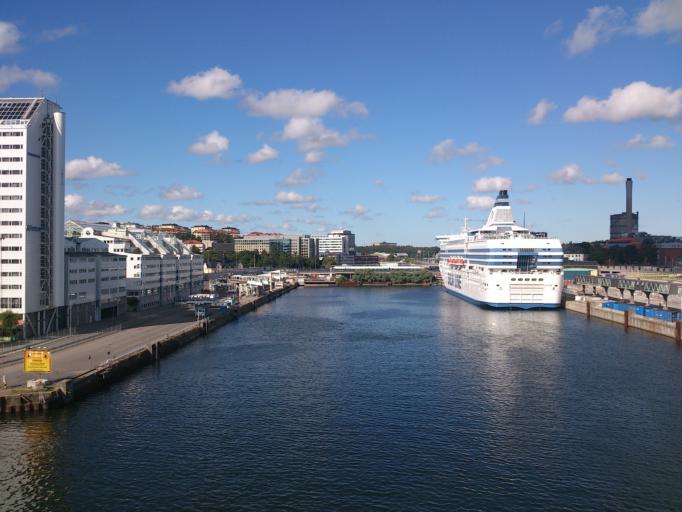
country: SE
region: Stockholm
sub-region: Lidingo
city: Lidingoe
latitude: 59.3497
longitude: 18.1164
